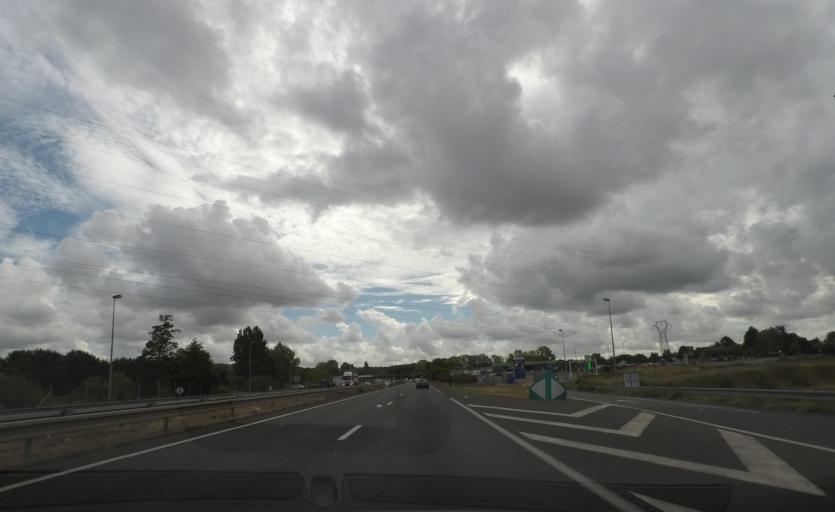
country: FR
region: Pays de la Loire
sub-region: Departement de Maine-et-Loire
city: Ecouflant
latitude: 47.5014
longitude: -0.4929
